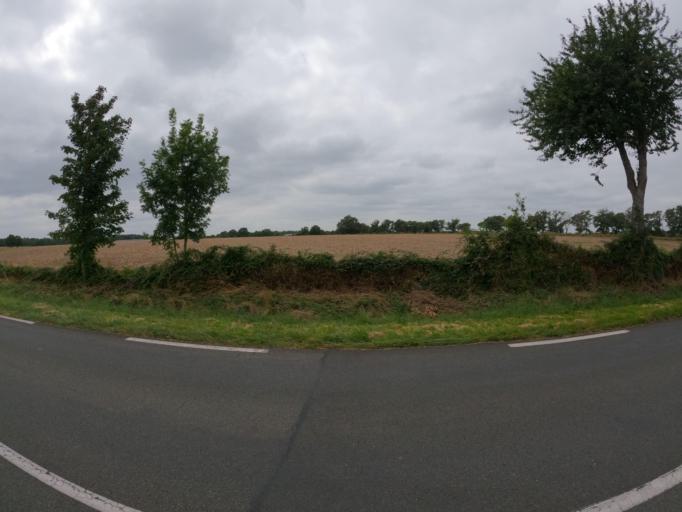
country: FR
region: Poitou-Charentes
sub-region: Departement de la Charente
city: Confolens
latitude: 46.0557
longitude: 0.6114
